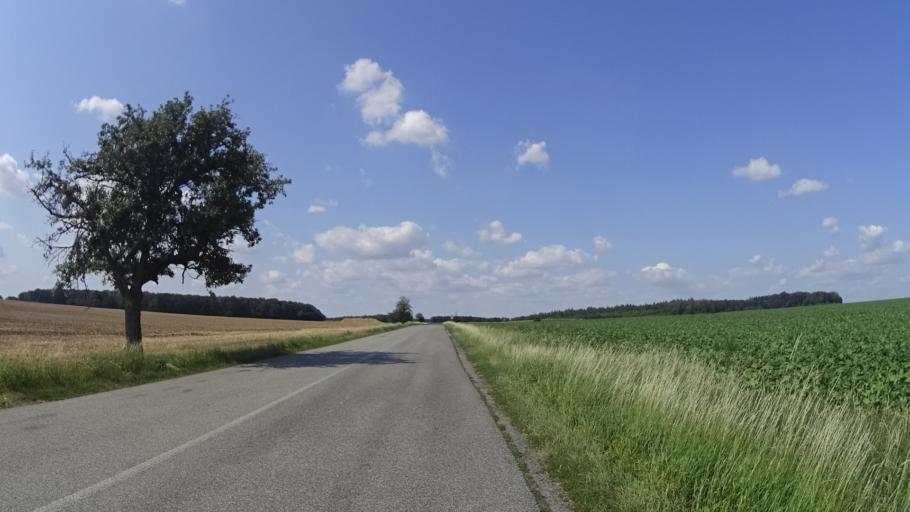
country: CZ
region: Kralovehradecky
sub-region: Okres Jicin
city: Jicin
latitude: 50.3682
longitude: 15.3691
